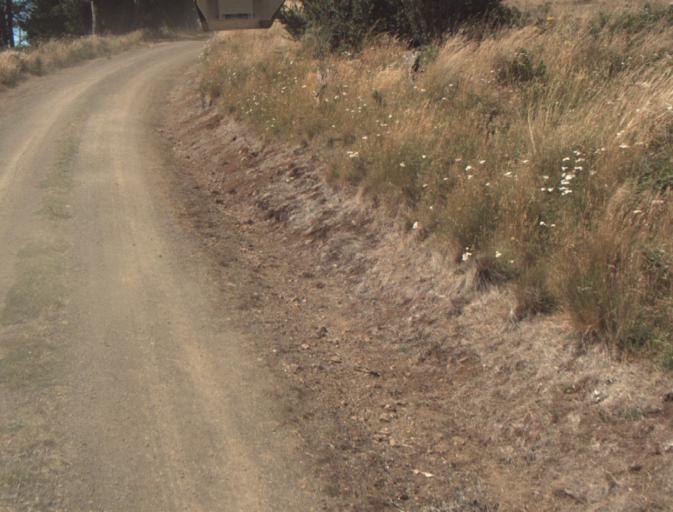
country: AU
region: Tasmania
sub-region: Dorset
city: Scottsdale
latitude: -41.3469
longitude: 147.4540
